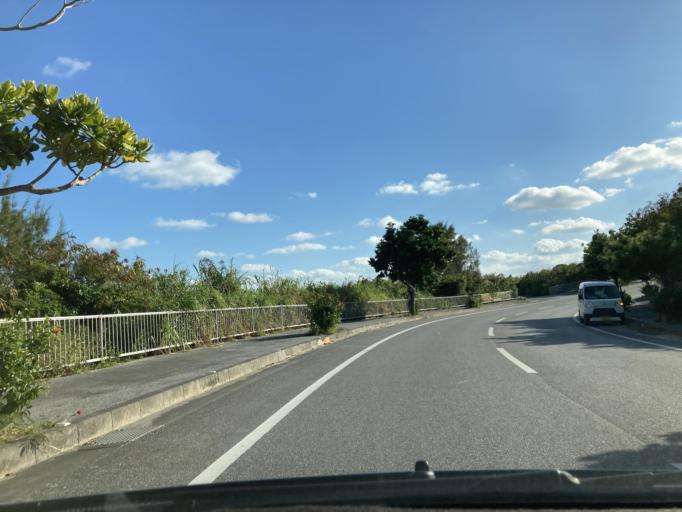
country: JP
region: Okinawa
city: Katsuren-haebaru
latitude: 26.3063
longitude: 127.9209
